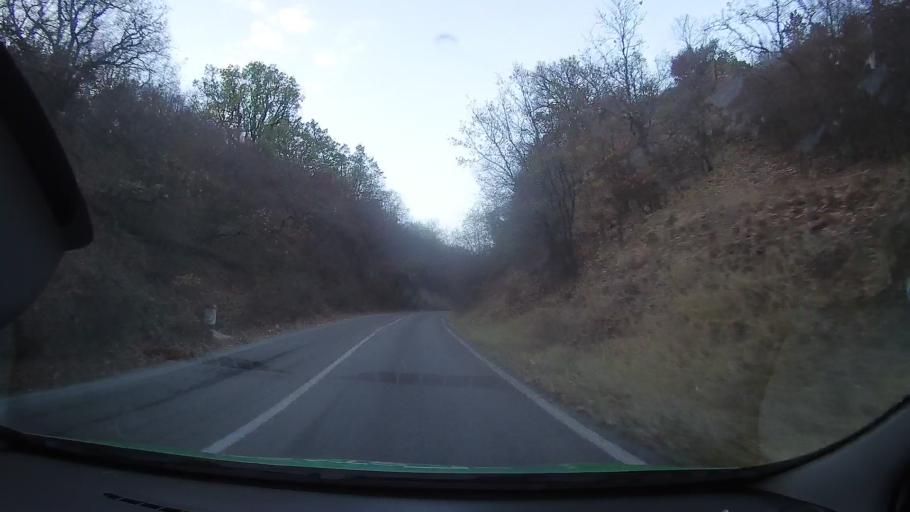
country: RO
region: Constanta
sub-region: Comuna Baneasa
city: Baneasa
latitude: 44.0896
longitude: 27.6546
